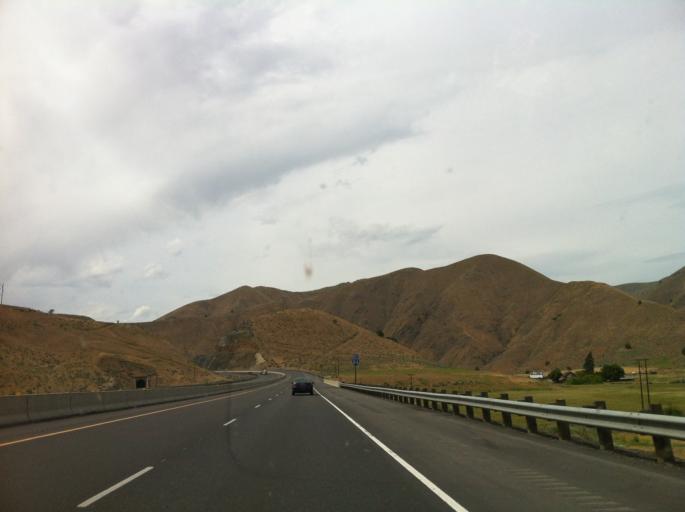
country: US
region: Idaho
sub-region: Washington County
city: Weiser
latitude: 44.4358
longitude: -117.3220
